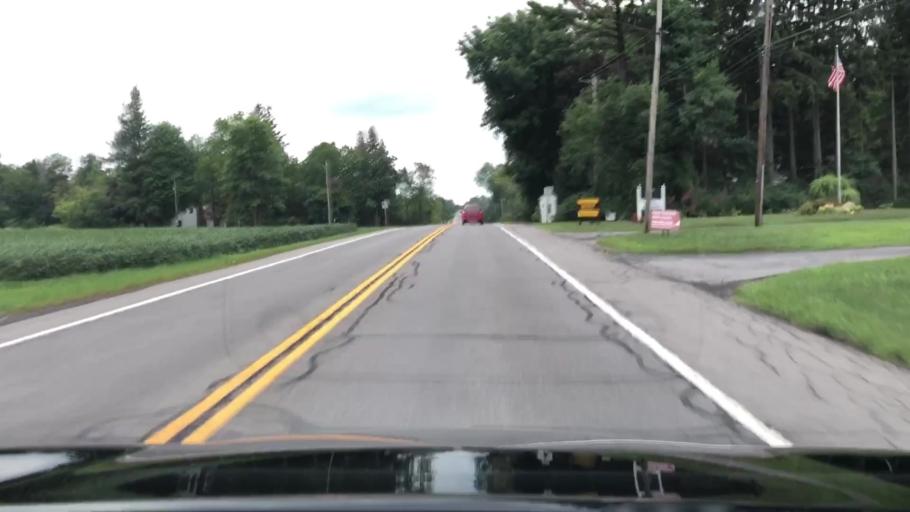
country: US
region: New York
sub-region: Erie County
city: Orchard Park
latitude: 42.7818
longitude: -78.6970
